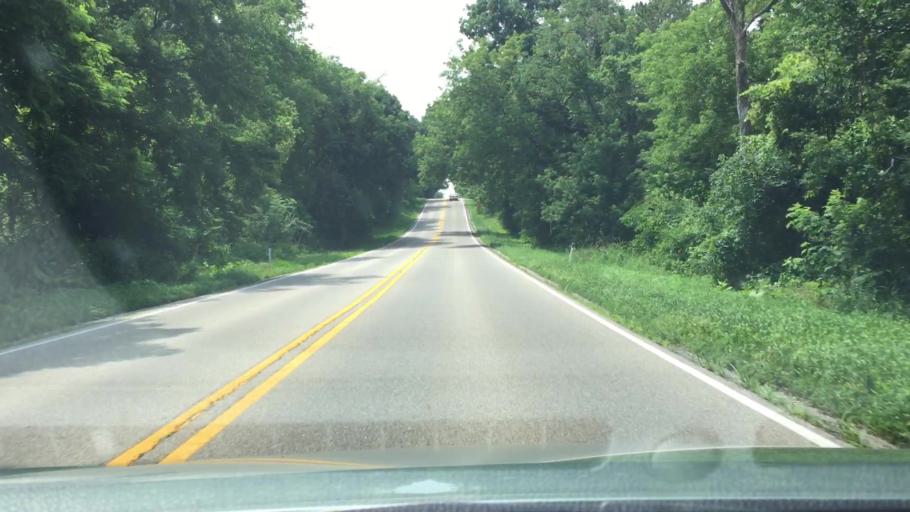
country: US
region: Wisconsin
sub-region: Waukesha County
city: Merton
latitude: 43.1288
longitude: -88.3077
